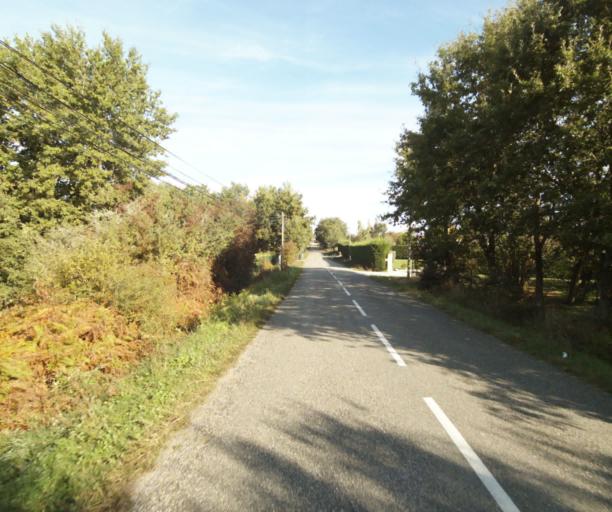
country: FR
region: Midi-Pyrenees
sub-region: Departement du Tarn-et-Garonne
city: Nohic
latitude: 43.9209
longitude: 1.4628
